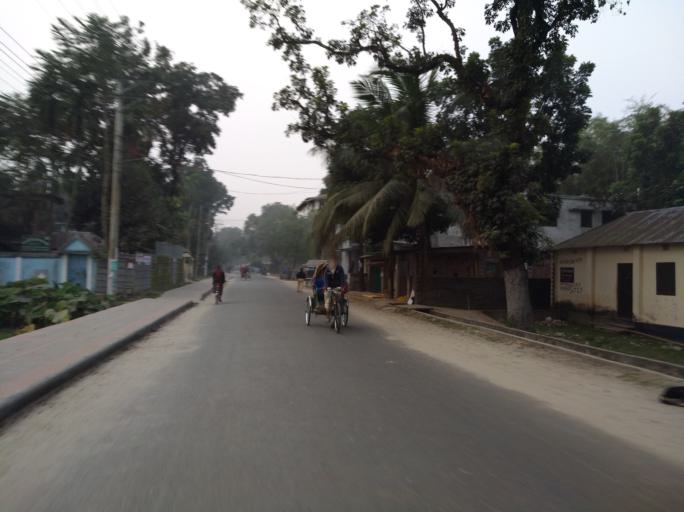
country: BD
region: Rajshahi
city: Saidpur
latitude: 25.9282
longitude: 88.8628
